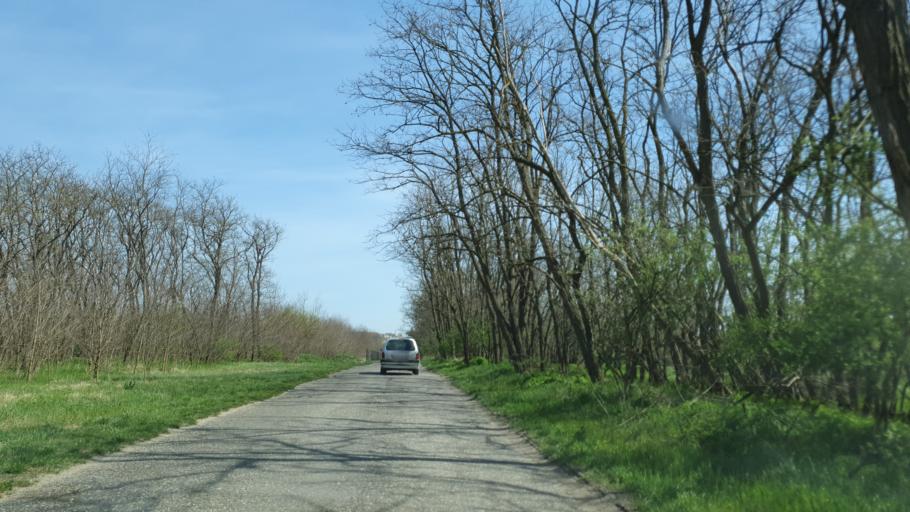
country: HU
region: Komarom-Esztergom
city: Oroszlany
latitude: 47.4951
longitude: 18.2920
